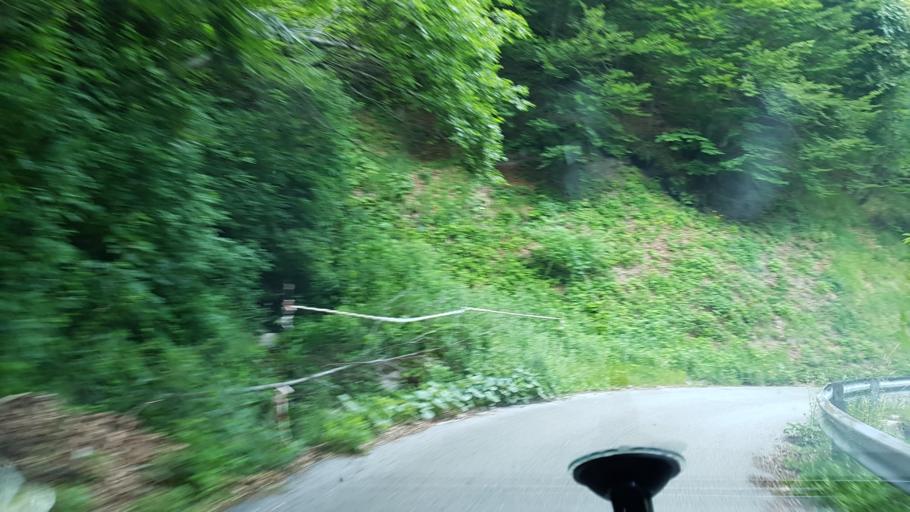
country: IT
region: Friuli Venezia Giulia
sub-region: Provincia di Udine
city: Prato
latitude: 46.3283
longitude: 13.3633
